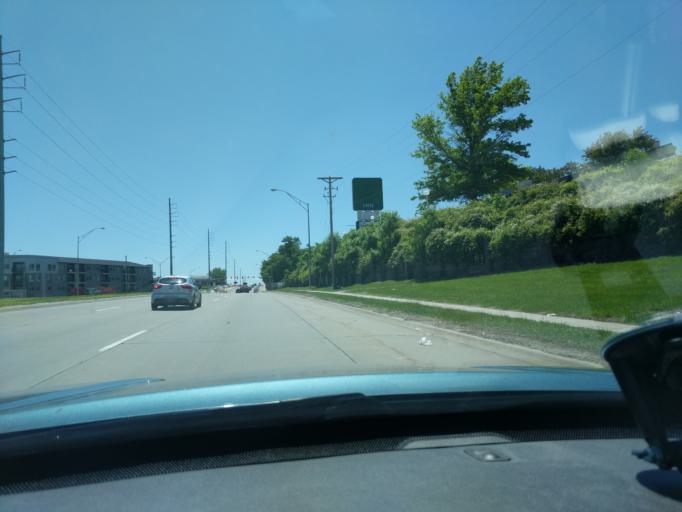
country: US
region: Nebraska
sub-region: Douglas County
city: Ralston
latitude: 41.2337
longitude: -96.0241
